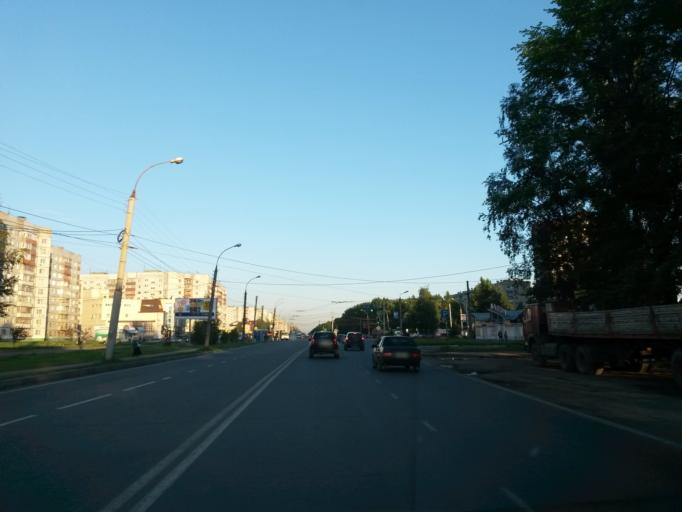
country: RU
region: Jaroslavl
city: Yaroslavl
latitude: 57.6970
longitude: 39.7656
